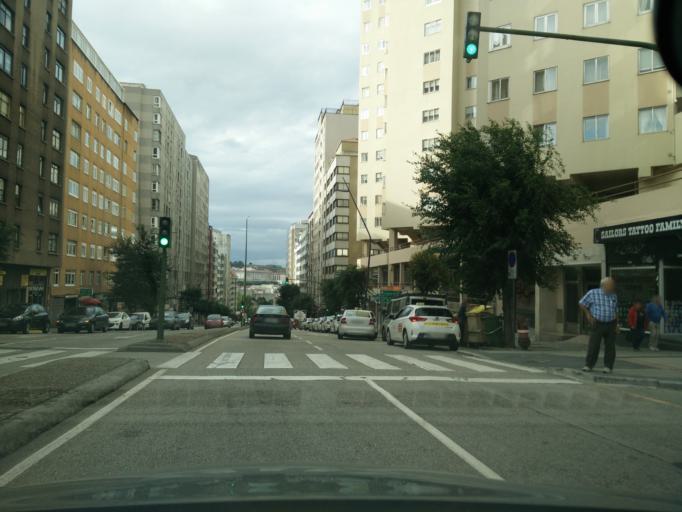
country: ES
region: Galicia
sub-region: Provincia da Coruna
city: A Coruna
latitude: 43.3626
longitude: -8.4225
